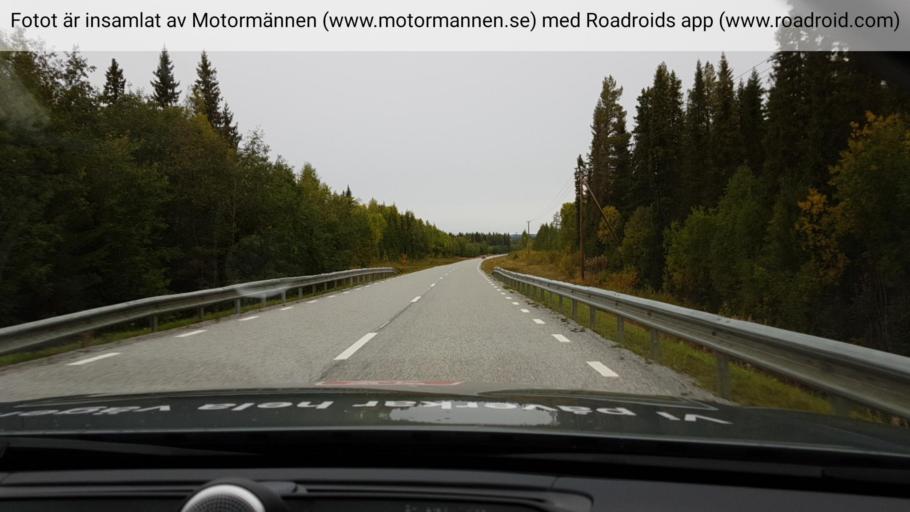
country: SE
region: Jaemtland
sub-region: Stroemsunds Kommun
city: Stroemsund
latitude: 63.9367
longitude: 15.4934
